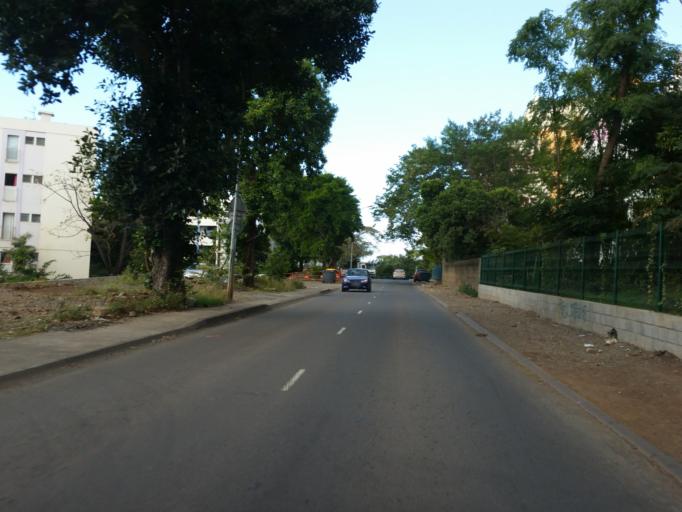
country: RE
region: Reunion
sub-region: Reunion
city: Saint-Denis
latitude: -20.8975
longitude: 55.4640
